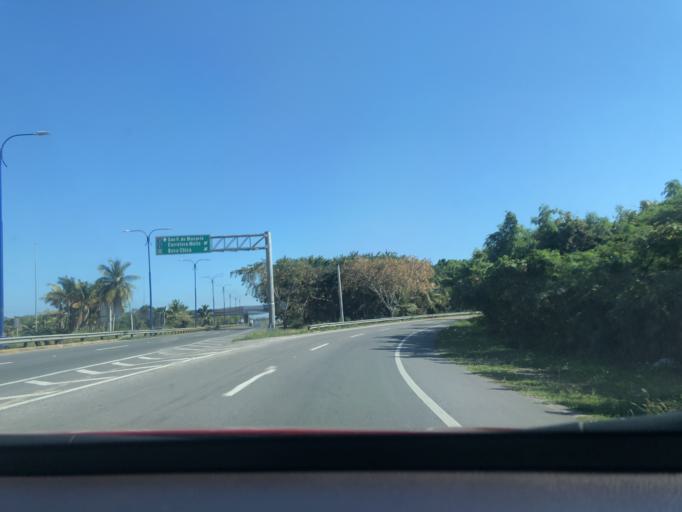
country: DO
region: Santo Domingo
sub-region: Santo Domingo
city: Boca Chica
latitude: 18.4520
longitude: -69.5978
